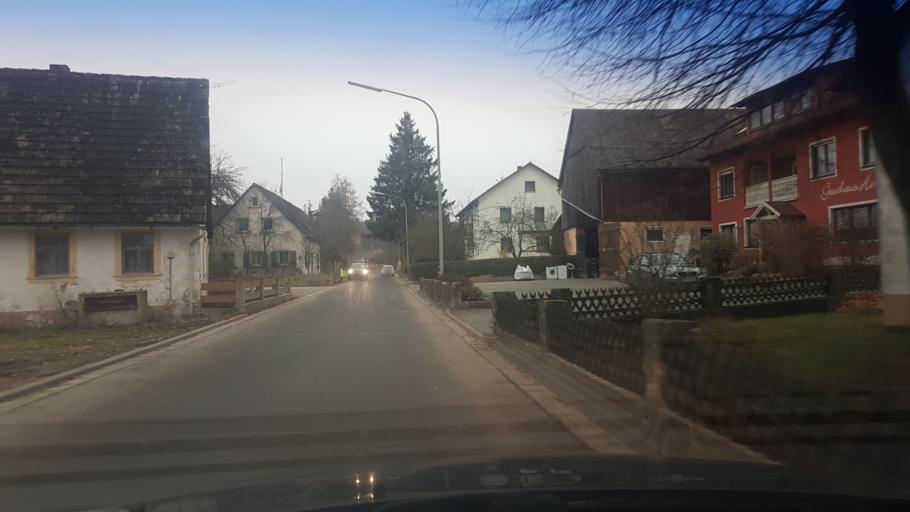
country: DE
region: Bavaria
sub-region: Upper Franconia
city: Weismain
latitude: 50.0316
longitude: 11.2664
